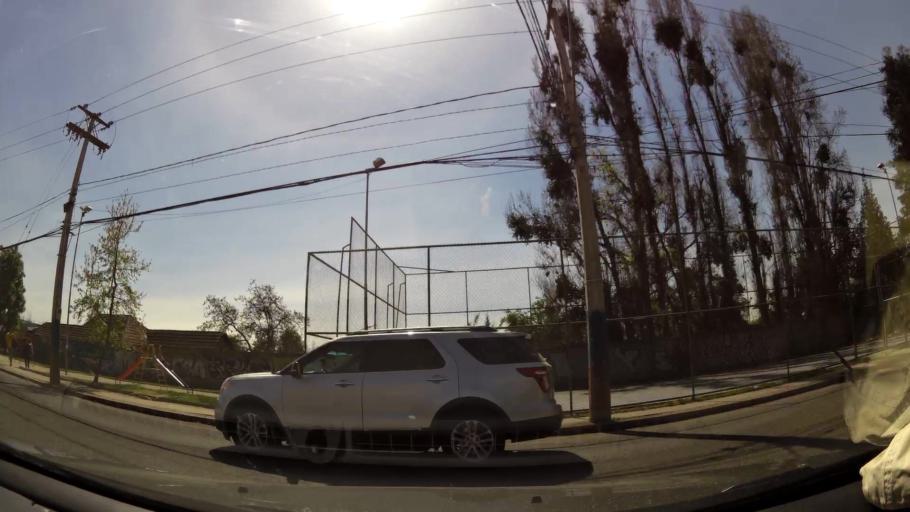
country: CL
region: Santiago Metropolitan
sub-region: Provincia de Cordillera
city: Puente Alto
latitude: -33.5620
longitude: -70.5637
